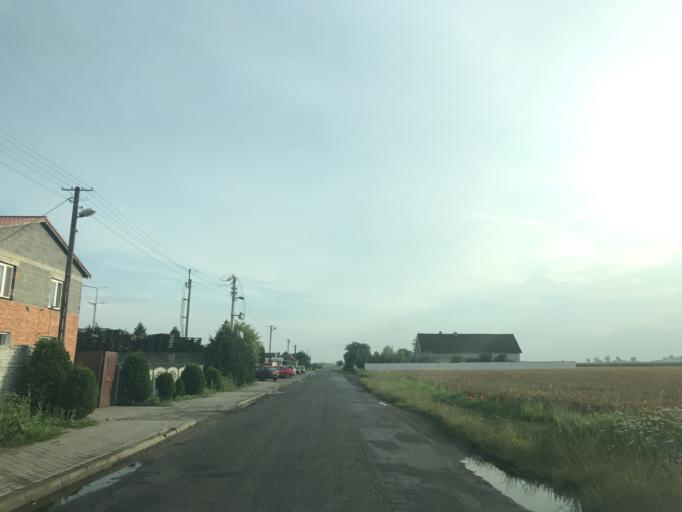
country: PL
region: Greater Poland Voivodeship
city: Miejska Gorka
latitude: 51.6363
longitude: 16.9604
